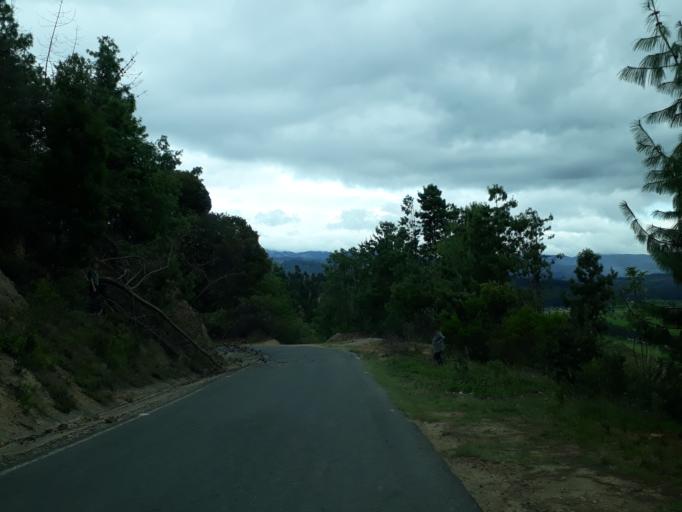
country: CO
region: Cundinamarca
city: Susa
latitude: 5.3996
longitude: -73.7719
